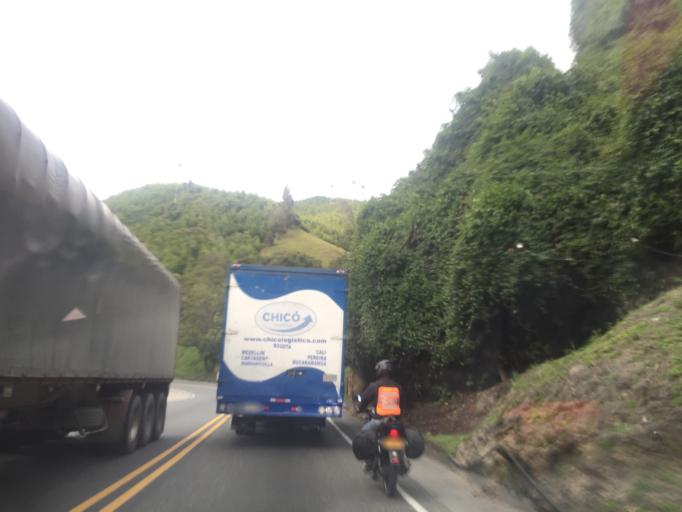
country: CO
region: Tolima
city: Cajamarca
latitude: 4.4550
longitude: -75.5313
